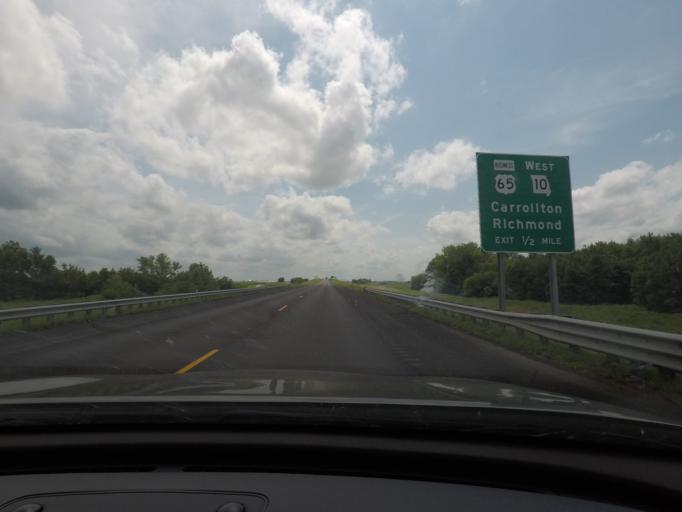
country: US
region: Missouri
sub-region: Carroll County
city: Carrollton
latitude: 39.3424
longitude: -93.4865
